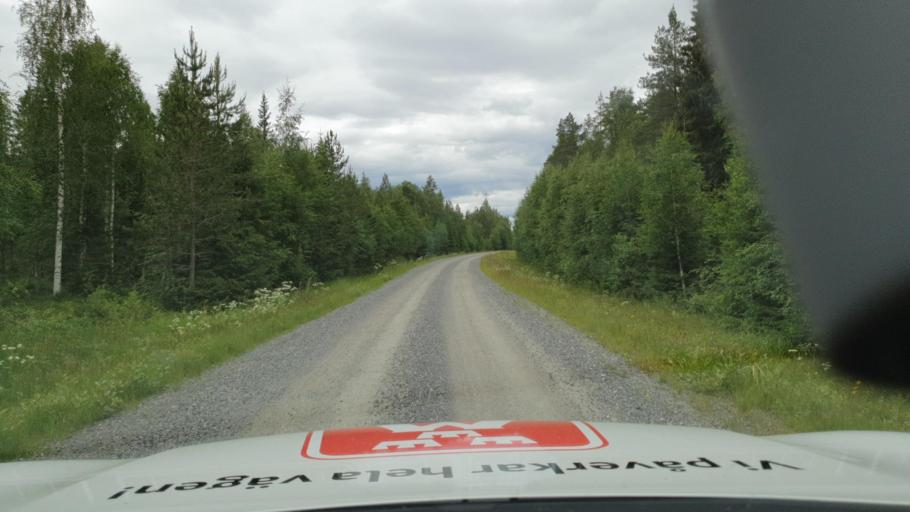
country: SE
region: Vaesterbotten
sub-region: Nordmalings Kommun
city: Nordmaling
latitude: 63.7397
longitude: 19.3895
